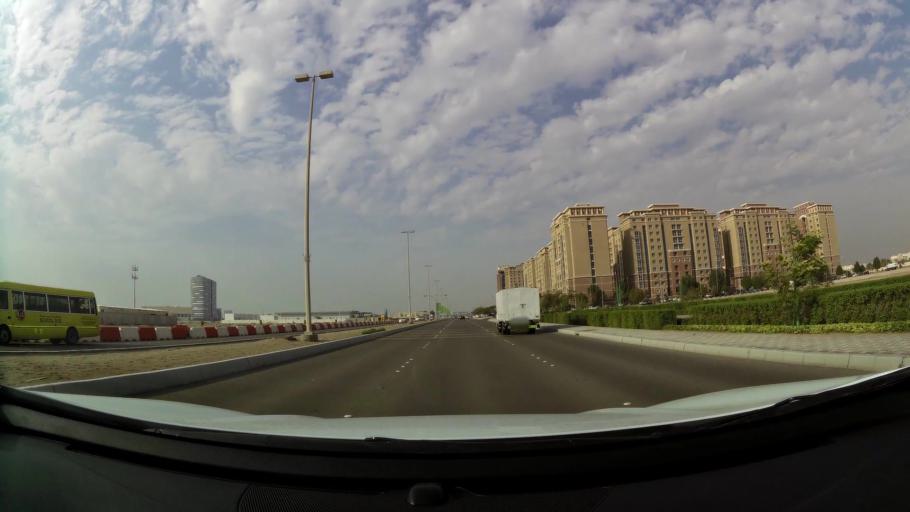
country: AE
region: Abu Dhabi
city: Abu Dhabi
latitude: 24.3689
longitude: 54.5356
